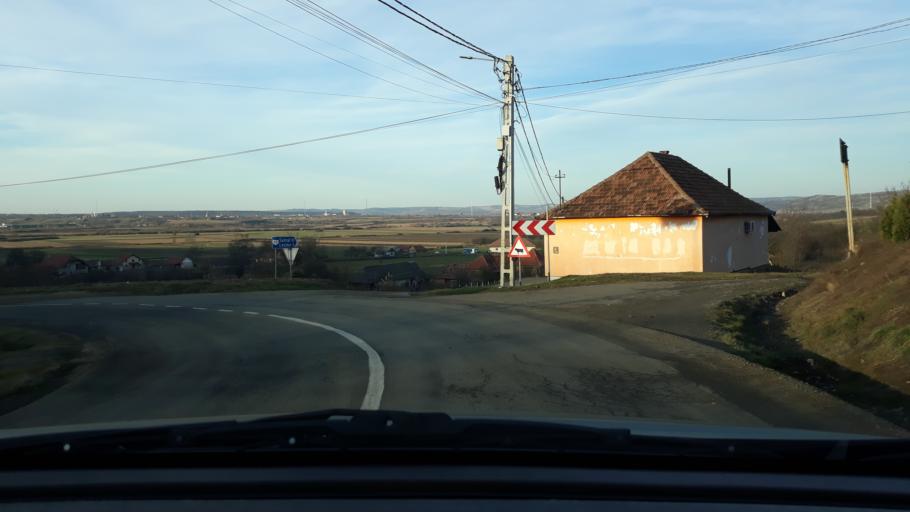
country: RO
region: Salaj
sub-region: Comuna Marca
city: Marca
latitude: 47.2290
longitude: 22.5521
